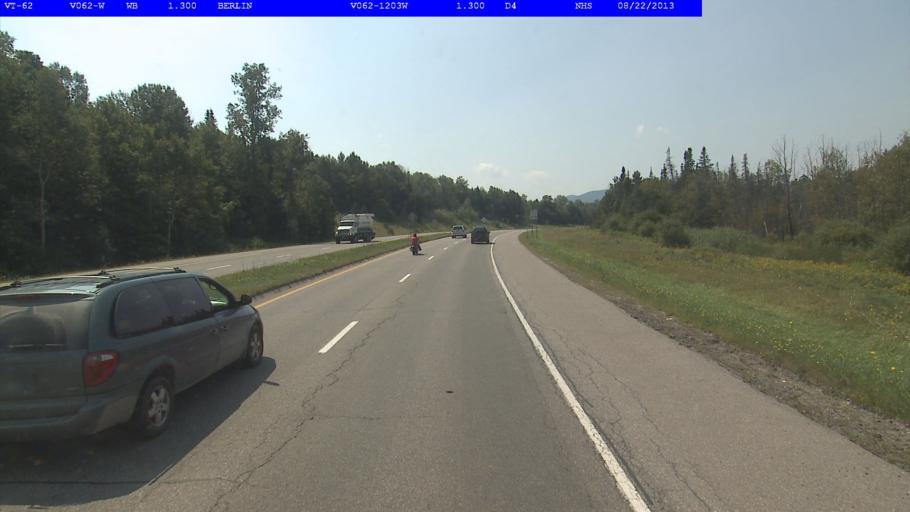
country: US
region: Vermont
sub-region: Washington County
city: Montpelier
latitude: 44.2170
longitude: -72.5608
